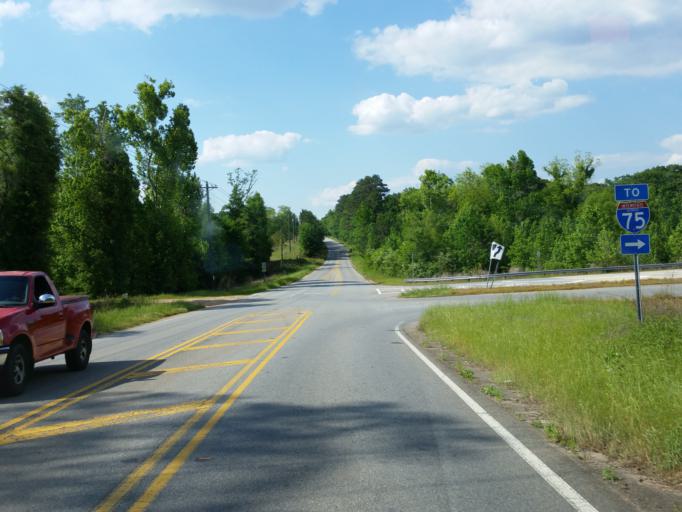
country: US
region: Georgia
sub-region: Peach County
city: Byron
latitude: 32.5861
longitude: -83.7483
